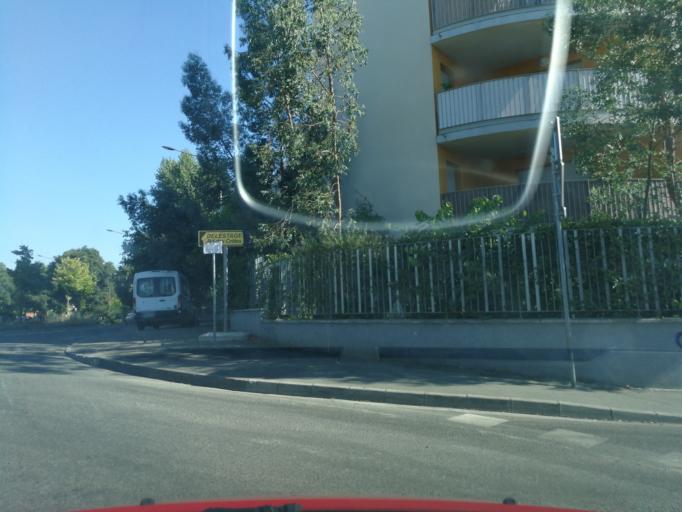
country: FR
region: Midi-Pyrenees
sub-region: Departement de la Haute-Garonne
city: Toulouse
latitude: 43.6232
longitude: 1.4542
